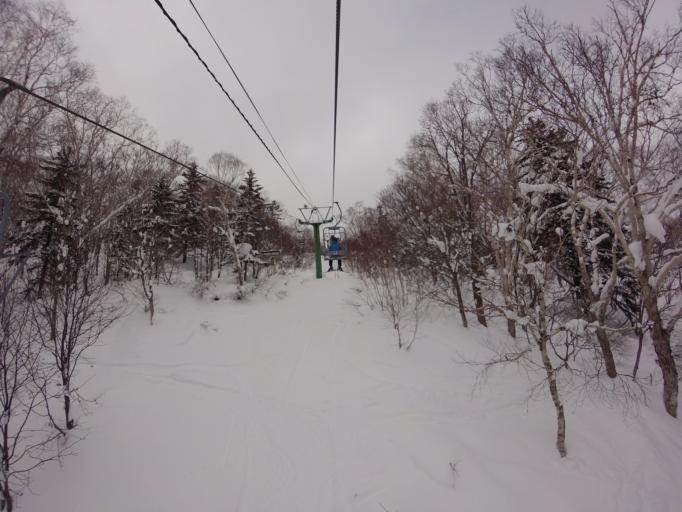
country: JP
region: Hokkaido
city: Sapporo
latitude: 43.0705
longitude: 141.2060
